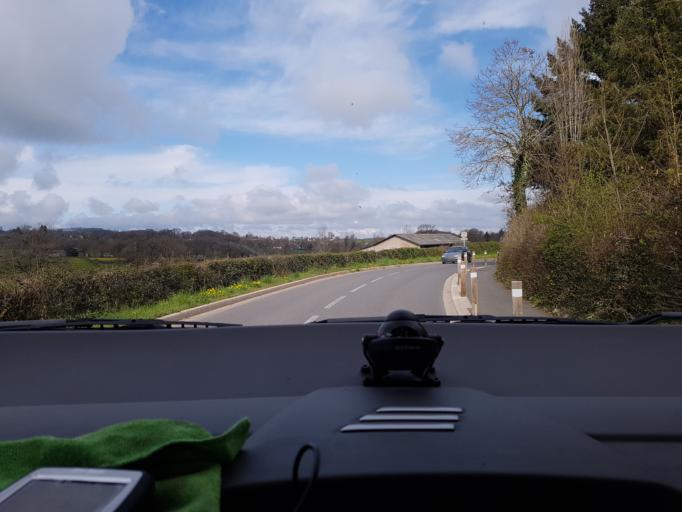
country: FR
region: Midi-Pyrenees
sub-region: Departement de l'Aveyron
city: Colombies
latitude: 44.4027
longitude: 2.2954
